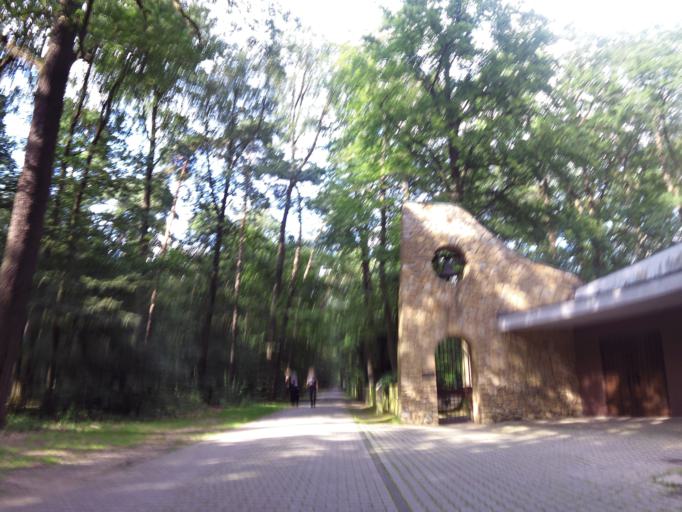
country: DE
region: Hesse
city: Niederrad
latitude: 50.0383
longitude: 8.6193
